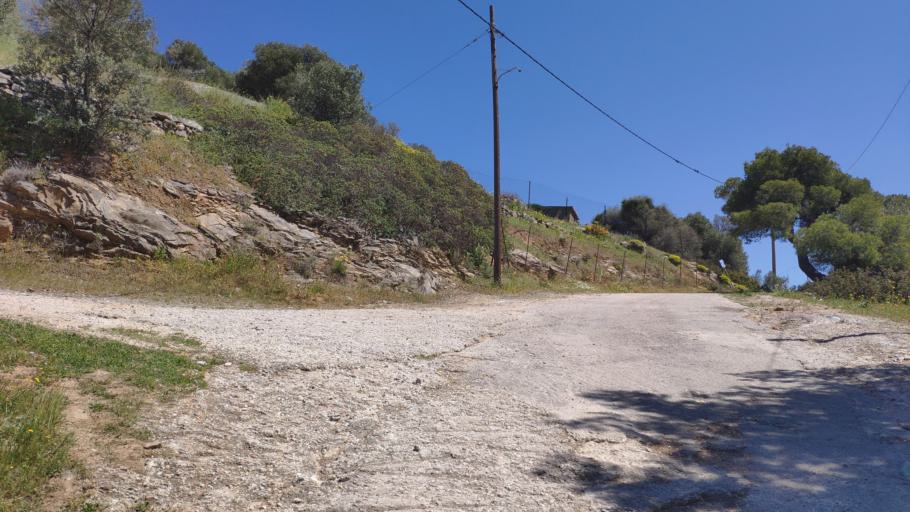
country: GR
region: Attica
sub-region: Nomarchia Anatolikis Attikis
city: Limin Mesoyaias
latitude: 37.8996
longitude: 24.0351
